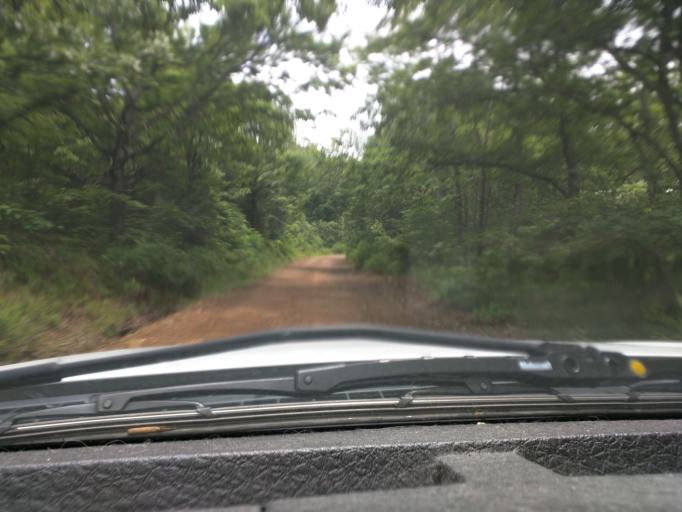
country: US
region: Arkansas
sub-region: Madison County
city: Huntsville
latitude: 35.8879
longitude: -93.5576
